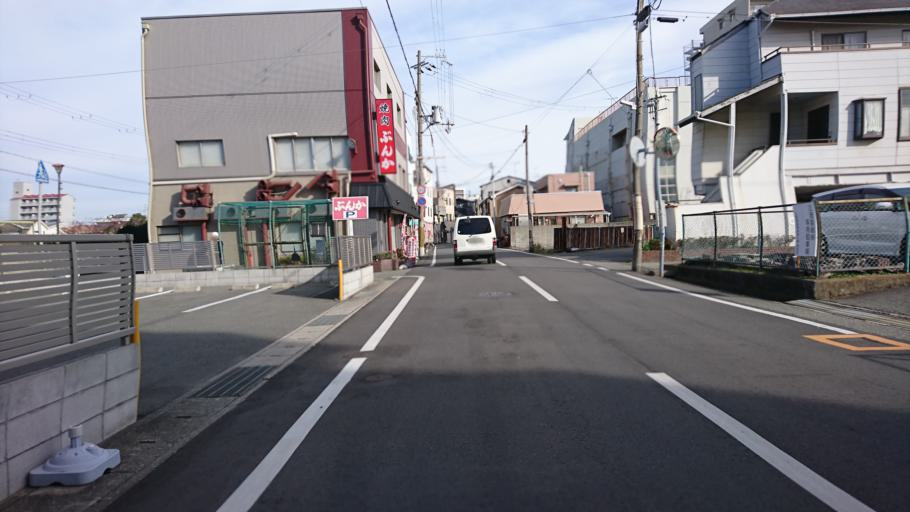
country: JP
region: Hyogo
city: Kakogawacho-honmachi
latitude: 34.7494
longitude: 134.8016
